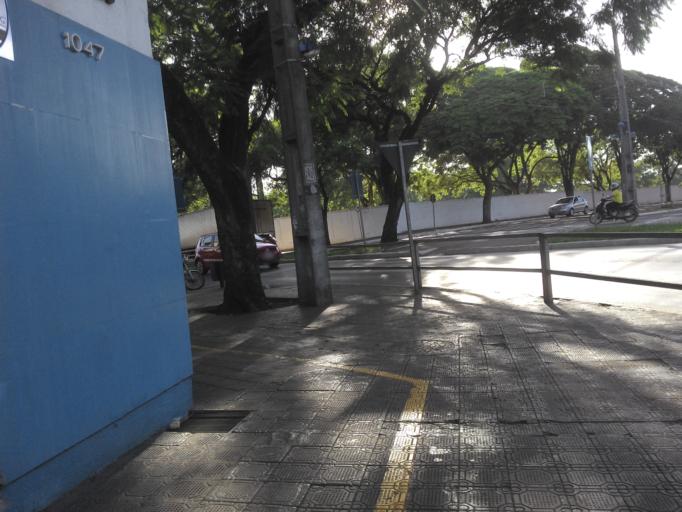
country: BR
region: Parana
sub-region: Maringa
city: Maringa
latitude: -23.4362
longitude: -51.9334
